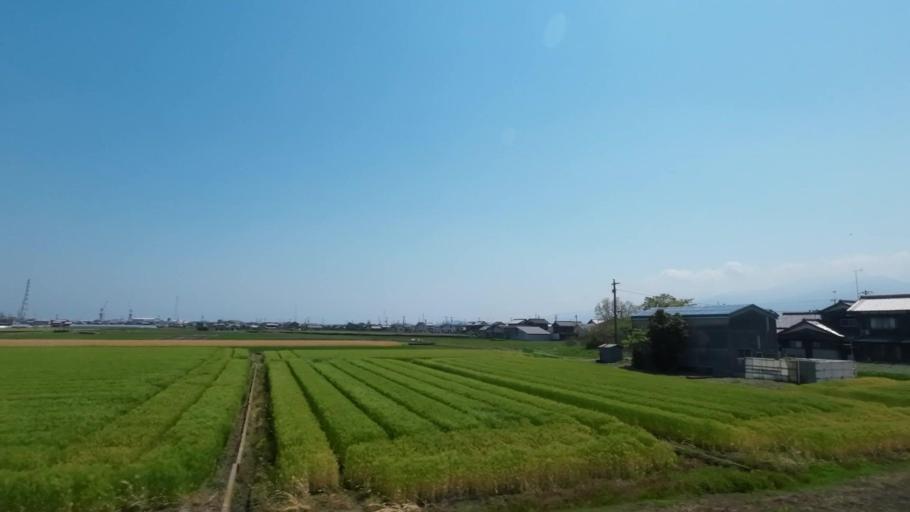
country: JP
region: Ehime
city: Saijo
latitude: 33.9143
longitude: 133.0987
